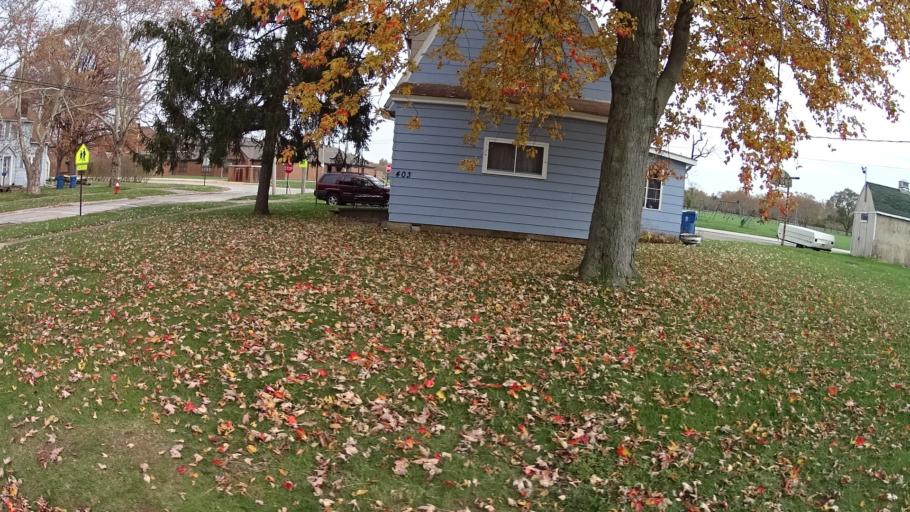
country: US
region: Ohio
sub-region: Lorain County
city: Lorain
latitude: 41.4729
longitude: -82.1560
